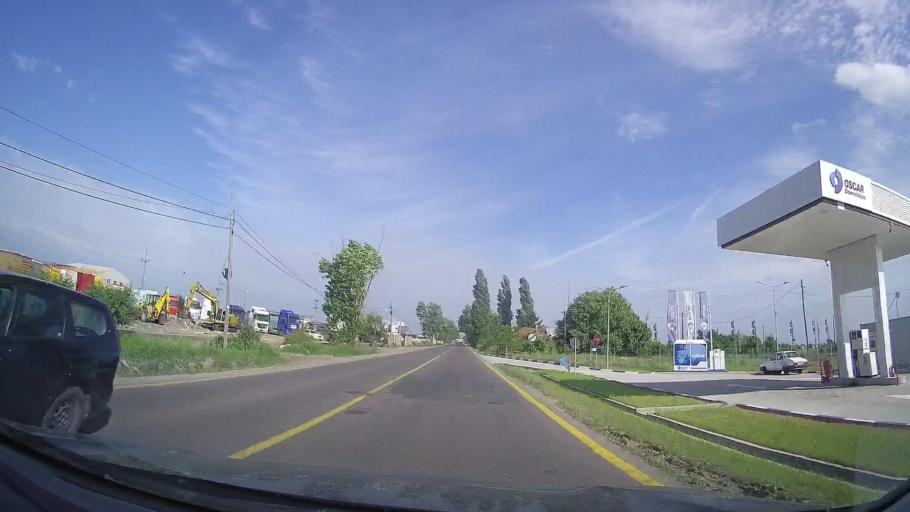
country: RO
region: Ilfov
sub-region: Comuna Magurele
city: Magurele
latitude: 44.3677
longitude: 26.0158
